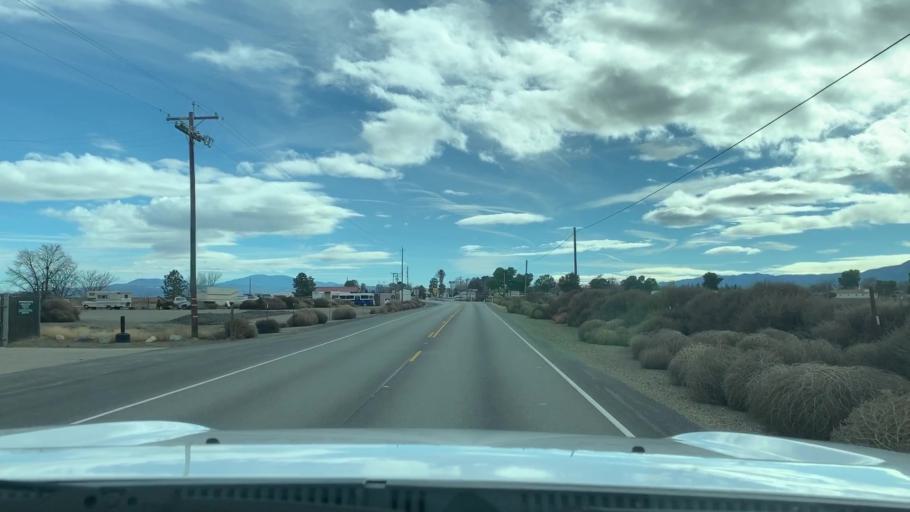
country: US
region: California
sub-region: Kern County
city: Taft Heights
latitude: 34.9506
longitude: -119.6958
